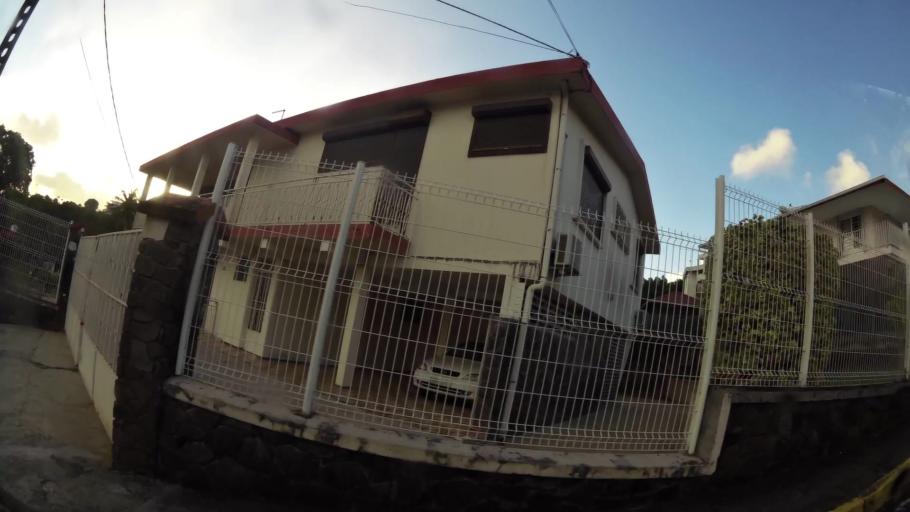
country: MQ
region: Martinique
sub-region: Martinique
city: Fort-de-France
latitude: 14.6214
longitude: -61.0708
